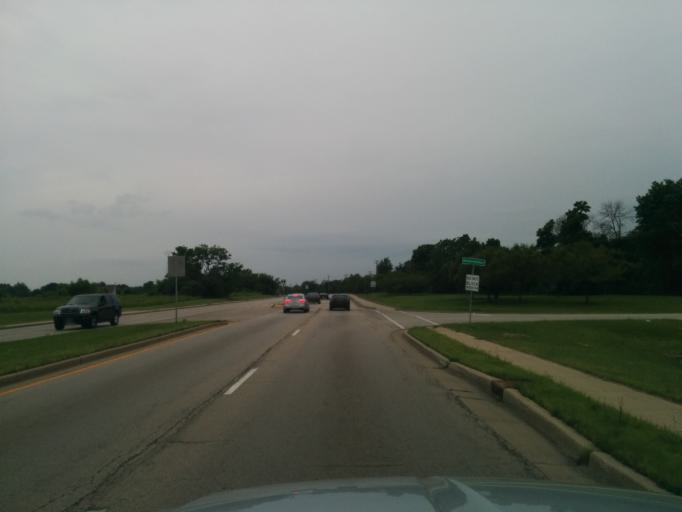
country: US
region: Illinois
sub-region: Kane County
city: Aurora
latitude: 41.7721
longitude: -88.2417
